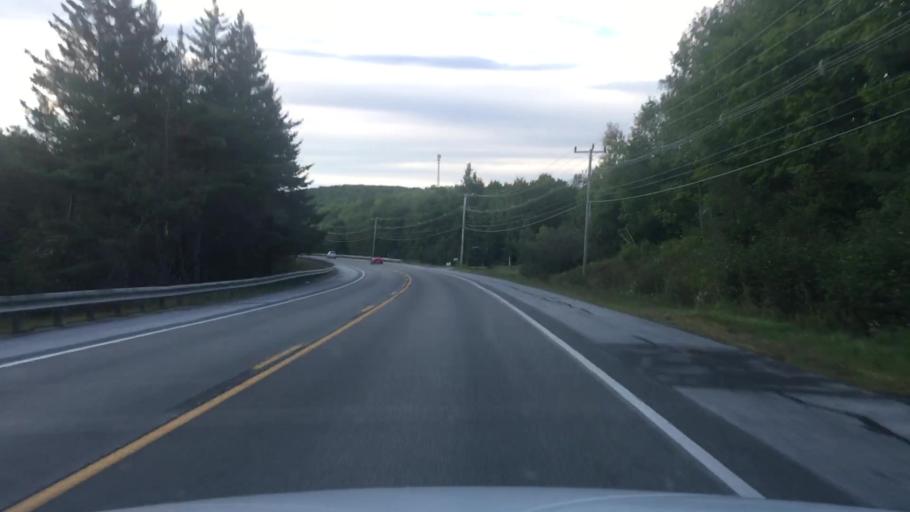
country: US
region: Maine
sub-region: Hancock County
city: Dedham
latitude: 44.7145
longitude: -68.6049
